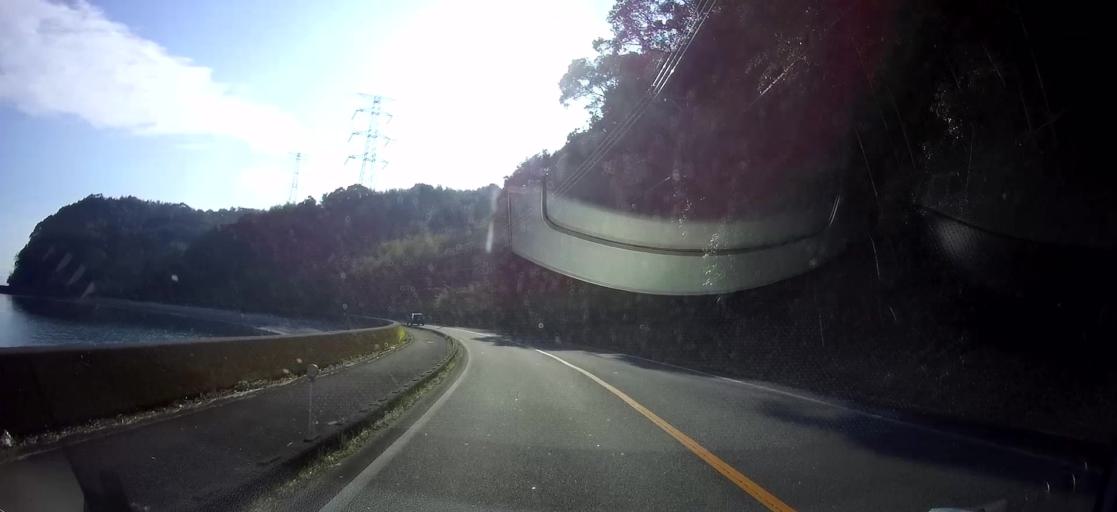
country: JP
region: Kumamoto
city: Yatsushiro
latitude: 32.5111
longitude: 130.4516
